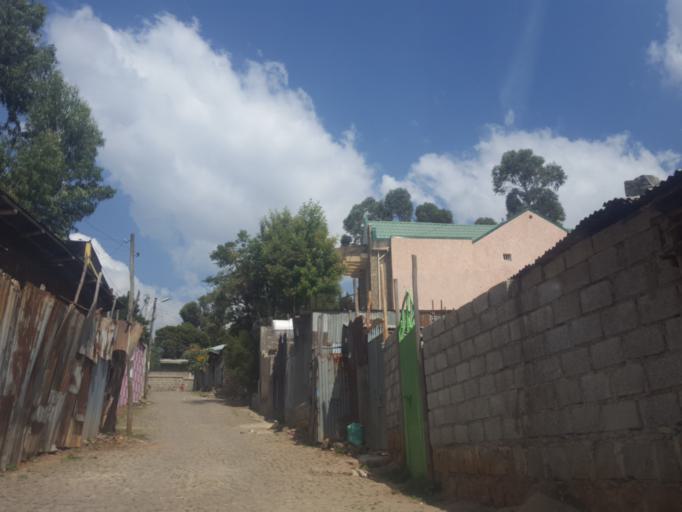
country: ET
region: Adis Abeba
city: Addis Ababa
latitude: 9.0565
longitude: 38.7281
